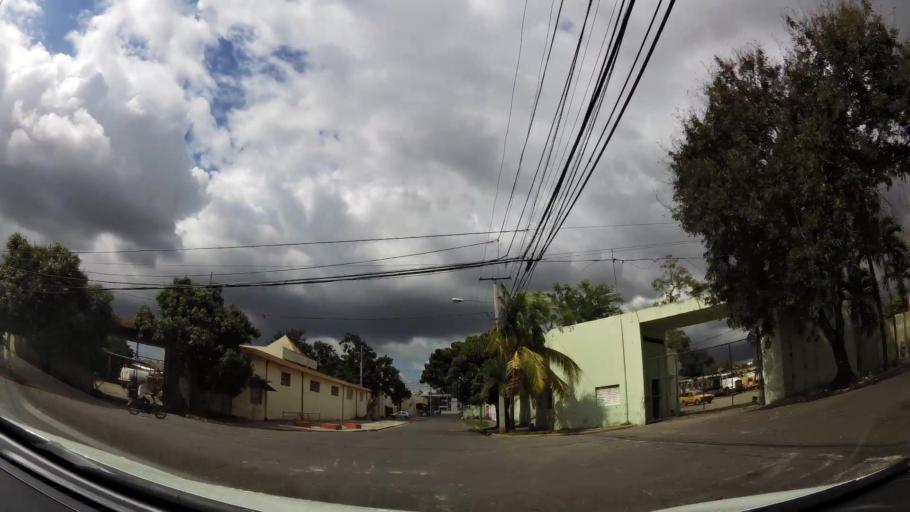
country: DO
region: Nacional
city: La Agustina
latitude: 18.4916
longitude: -69.9276
